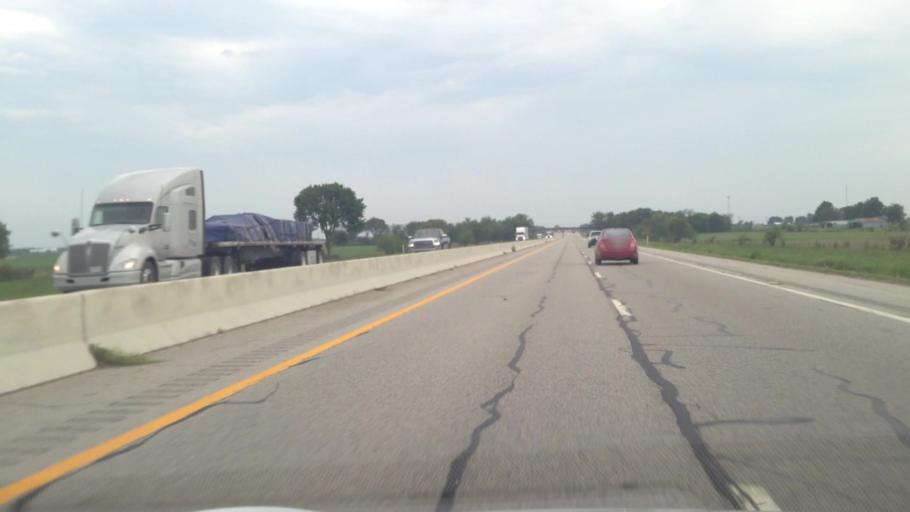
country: US
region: Oklahoma
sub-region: Ottawa County
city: Fairland
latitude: 36.7630
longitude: -94.8980
